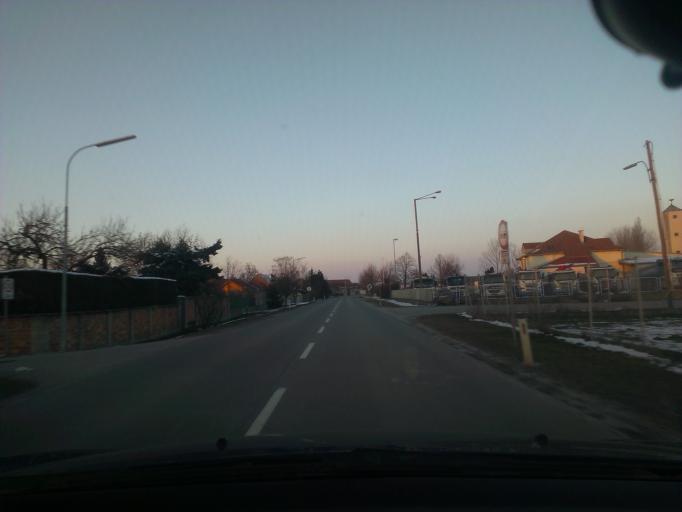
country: AT
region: Lower Austria
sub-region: Politischer Bezirk Baden
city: Reisenberg
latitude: 47.9948
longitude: 16.5230
